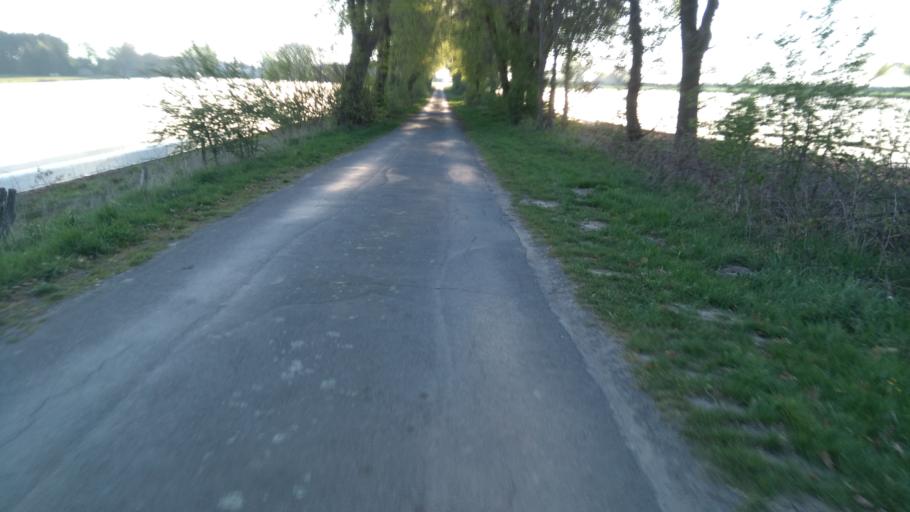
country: DE
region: Lower Saxony
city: Bliedersdorf
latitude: 53.4771
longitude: 9.5608
